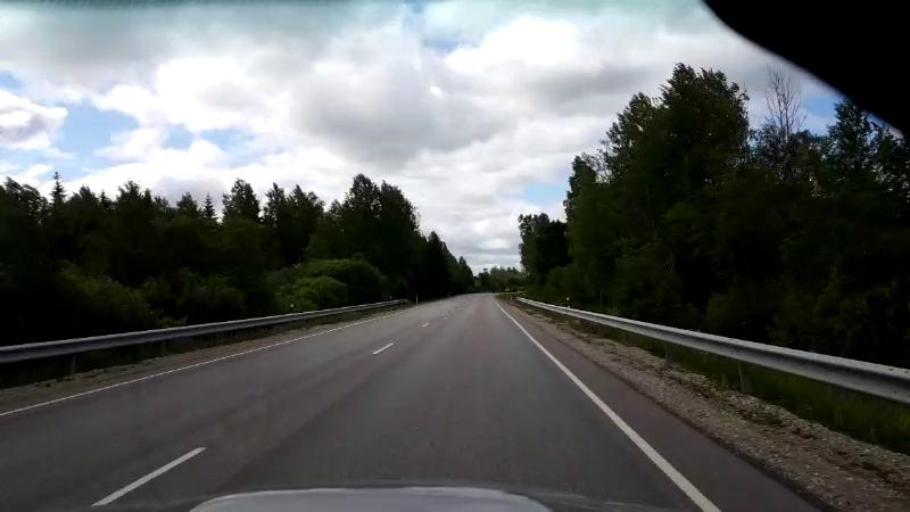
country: EE
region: Harju
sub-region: Nissi vald
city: Riisipere
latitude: 59.1028
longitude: 24.4715
